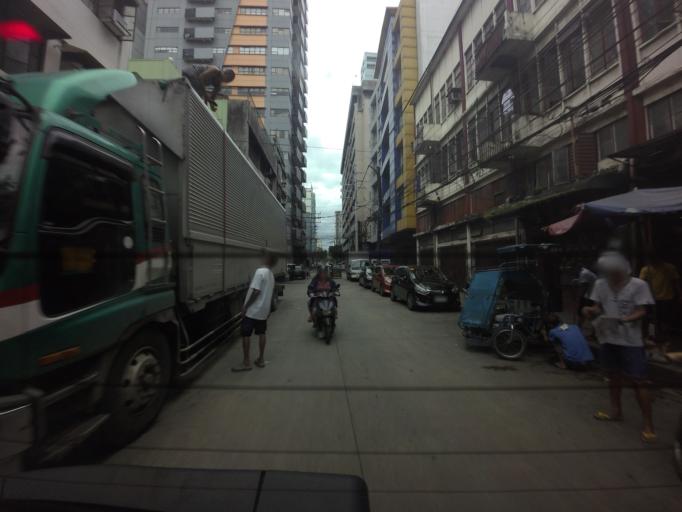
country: PH
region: Metro Manila
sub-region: City of Manila
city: Manila
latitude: 14.6011
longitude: 120.9692
